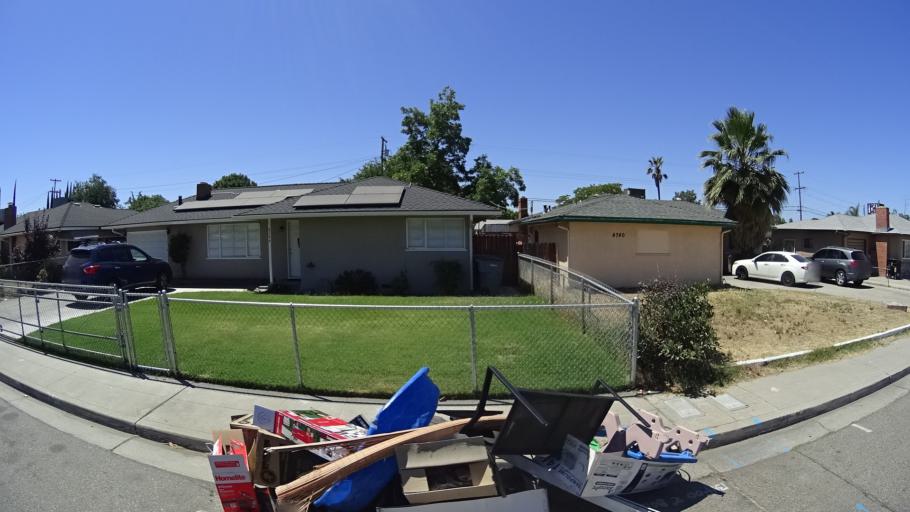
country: US
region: California
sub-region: Fresno County
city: Fresno
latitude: 36.7722
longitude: -119.7390
